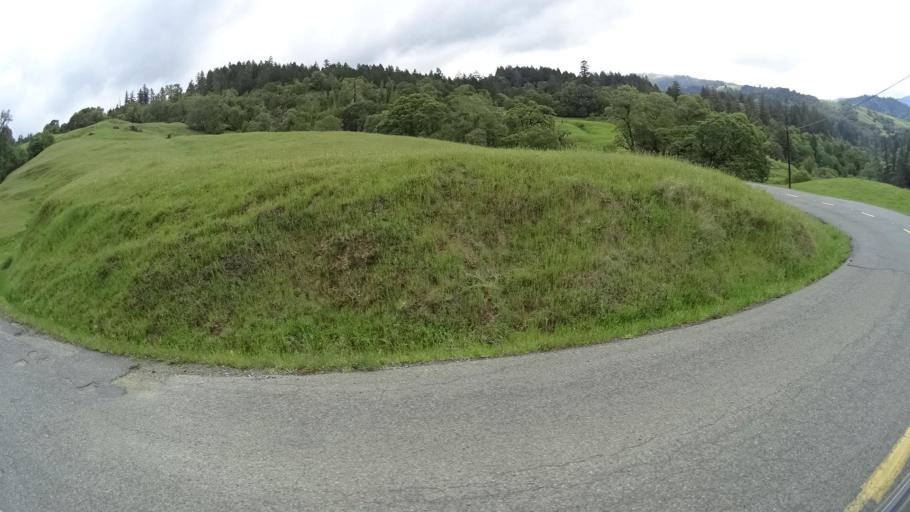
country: US
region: California
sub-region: Humboldt County
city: Redway
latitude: 40.2264
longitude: -123.6099
